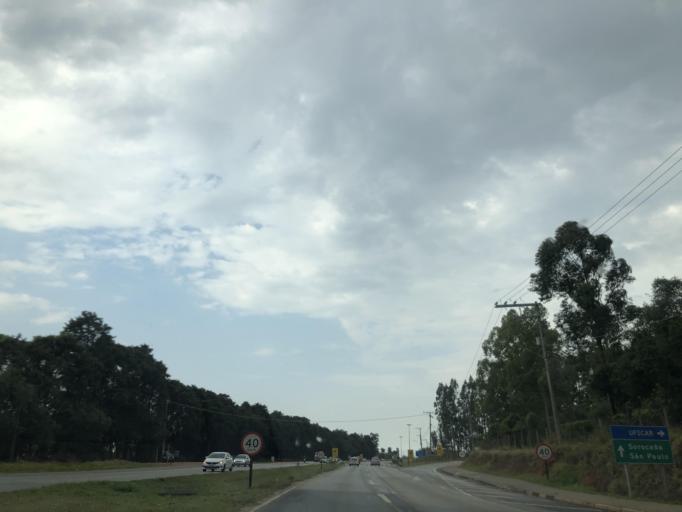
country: BR
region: Sao Paulo
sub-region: Salto De Pirapora
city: Salto de Pirapora
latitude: -23.5802
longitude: -47.5264
